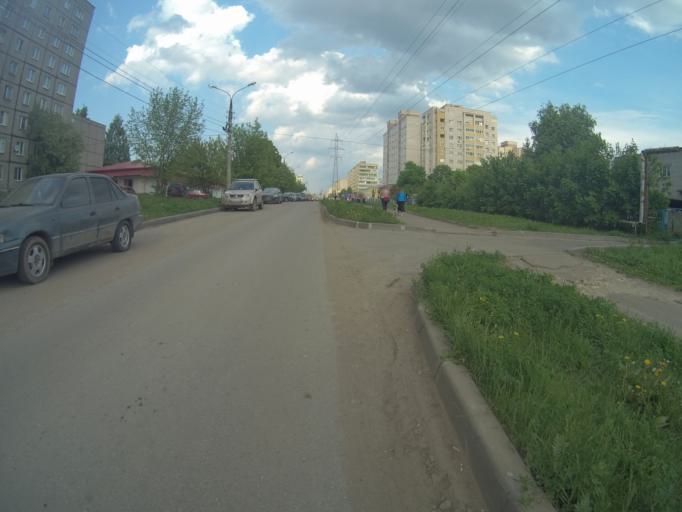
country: RU
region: Vladimir
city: Vladimir
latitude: 56.1698
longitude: 40.4387
